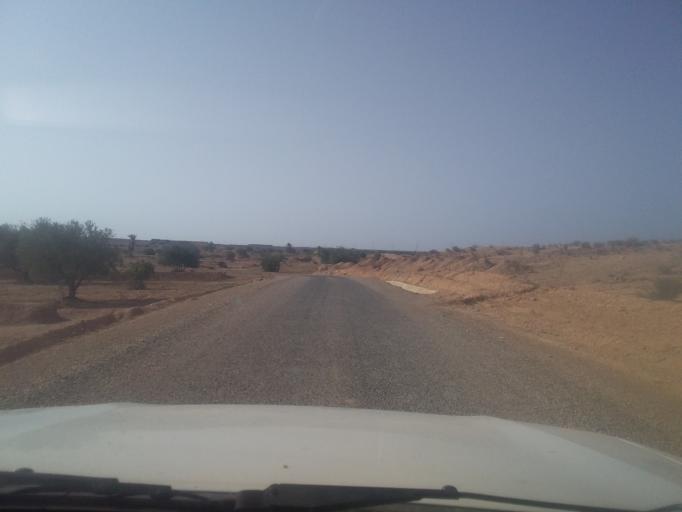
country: TN
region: Qabis
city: Matmata
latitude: 33.5845
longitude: 10.2593
